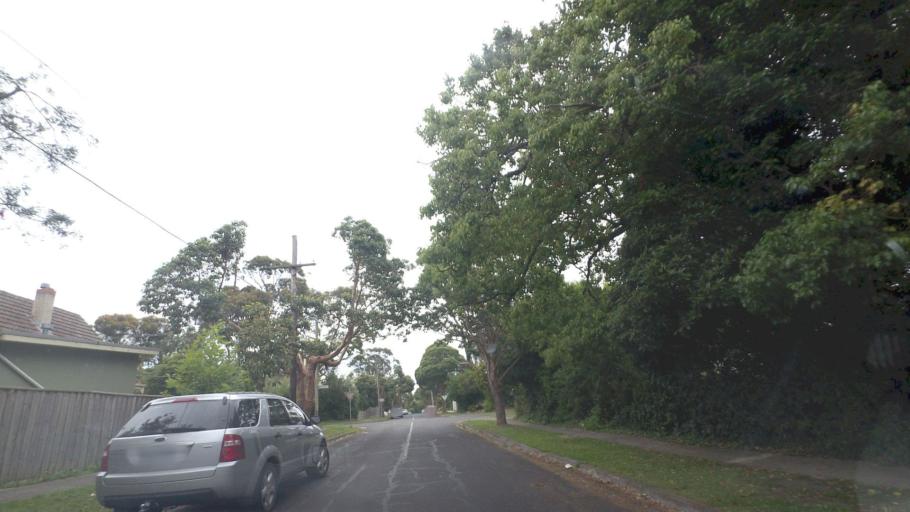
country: AU
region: Victoria
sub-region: Maroondah
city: Croydon North
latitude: -37.7965
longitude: 145.3004
